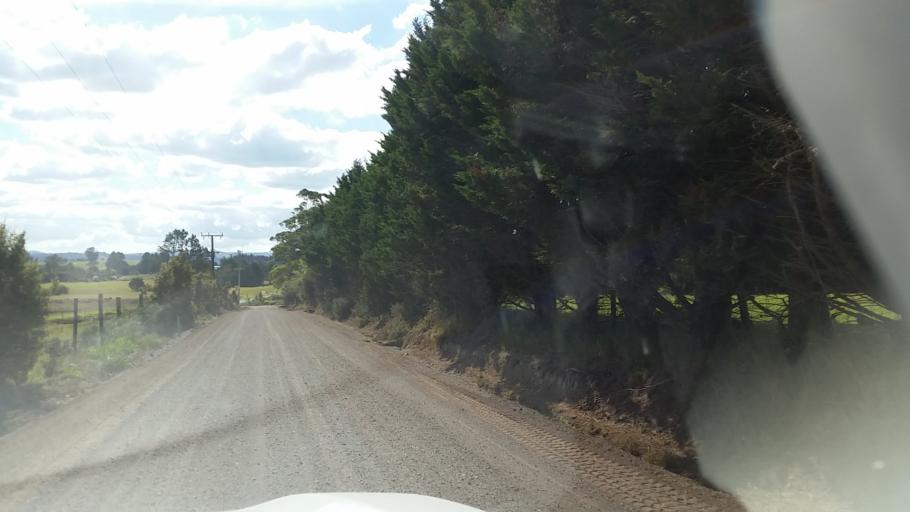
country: NZ
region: Northland
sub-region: Whangarei
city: Whangarei
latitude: -35.5823
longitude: 174.3112
